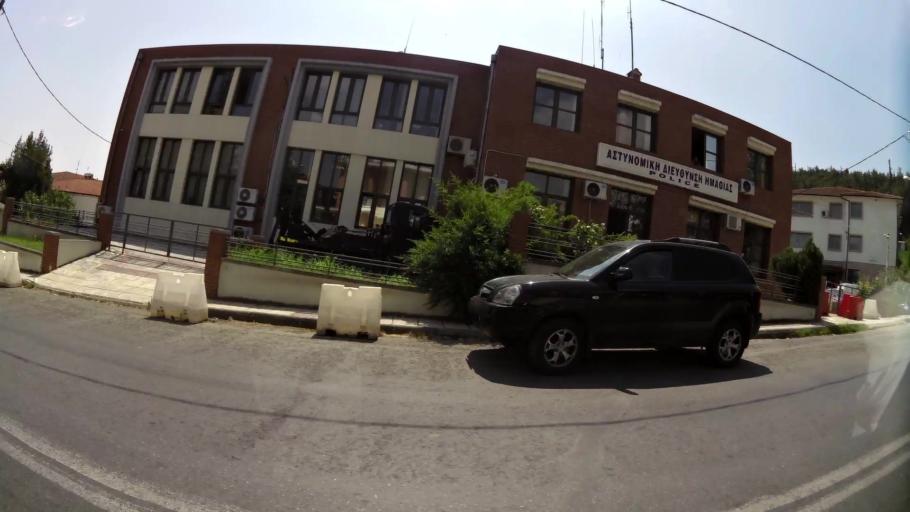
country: GR
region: Central Macedonia
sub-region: Nomos Imathias
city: Veroia
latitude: 40.5100
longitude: 22.2158
